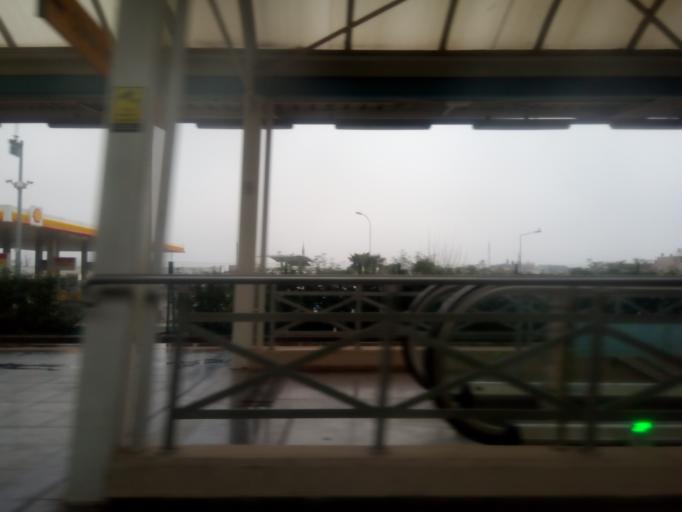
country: TR
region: Bursa
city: Yildirim
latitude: 40.2004
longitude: 29.0403
